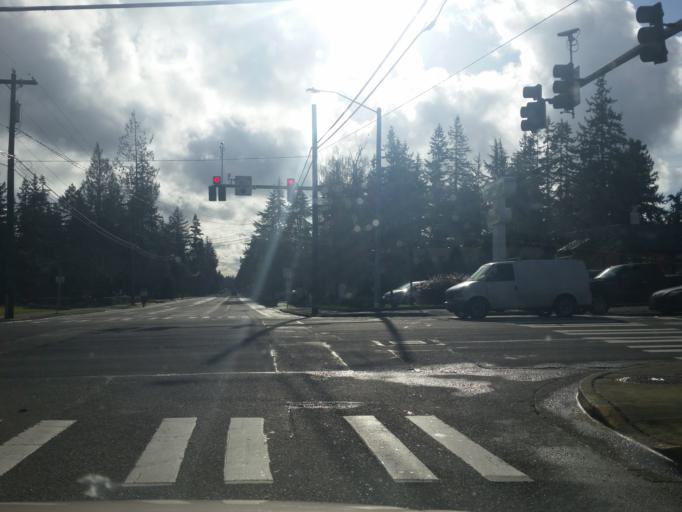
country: US
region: Washington
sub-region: Snohomish County
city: Lynnwood
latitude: 47.8216
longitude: -122.3251
